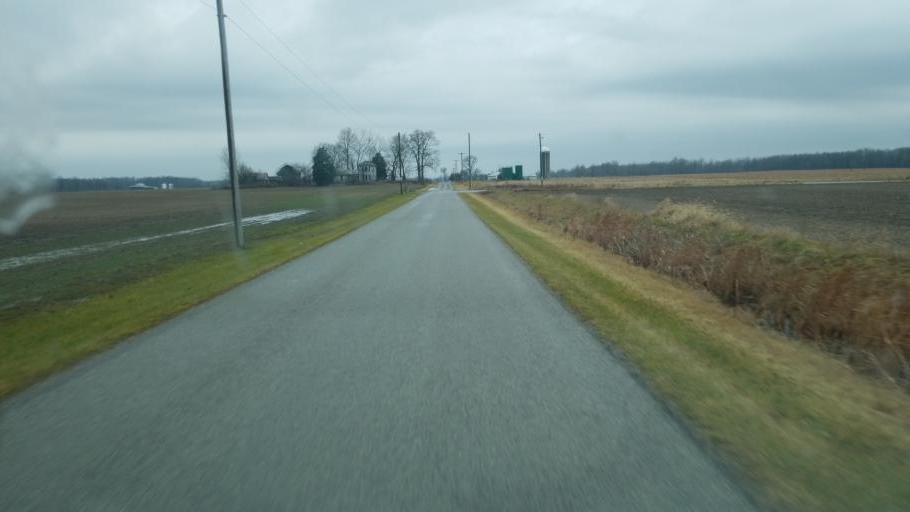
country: US
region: Ohio
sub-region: Morrow County
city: Cardington
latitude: 40.4373
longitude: -82.8711
